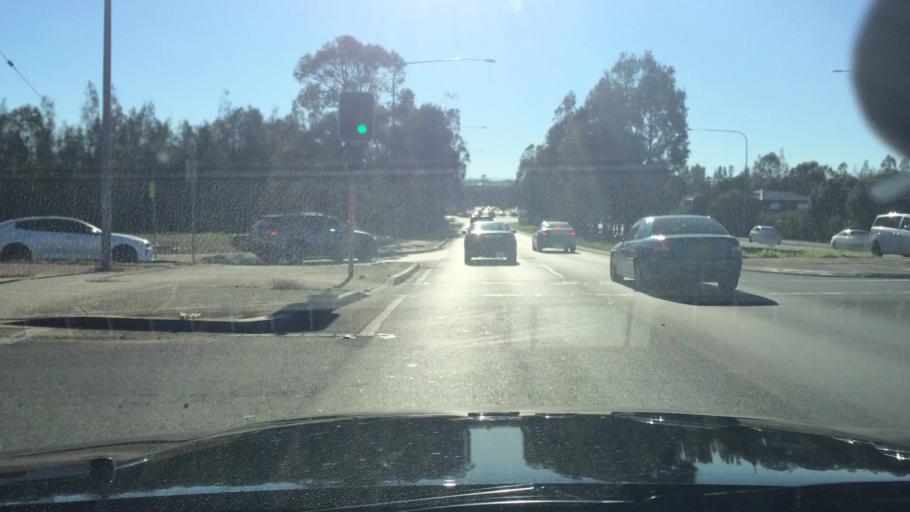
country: AU
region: New South Wales
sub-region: Liverpool
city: Miller
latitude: -33.9210
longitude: 150.8506
